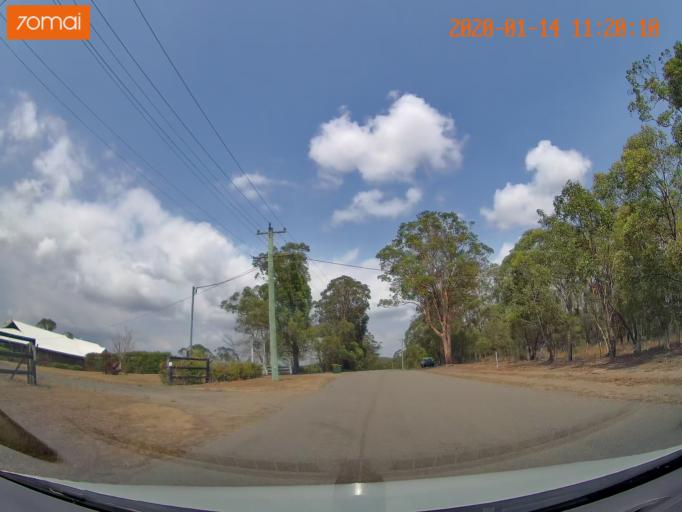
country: AU
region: New South Wales
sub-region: Lake Macquarie Shire
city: Cooranbong
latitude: -33.1009
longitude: 151.4572
